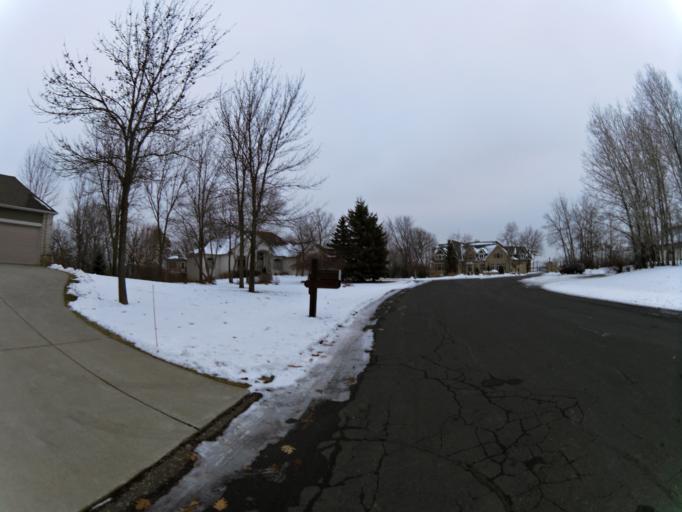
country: US
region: Minnesota
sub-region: Washington County
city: Lake Elmo
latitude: 44.9691
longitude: -92.8399
